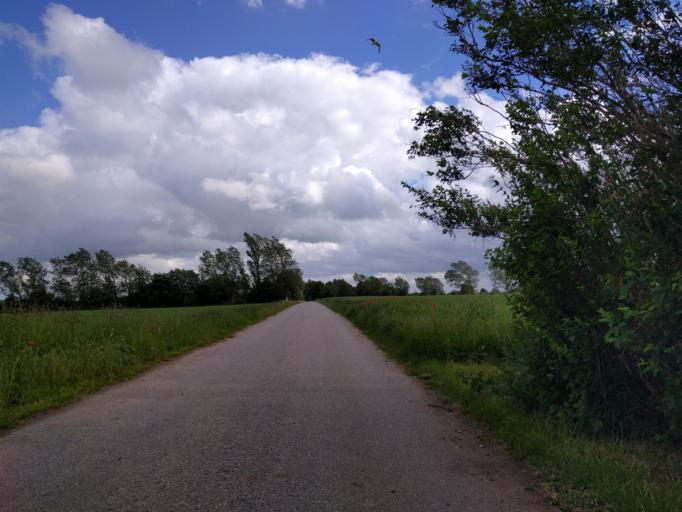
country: DK
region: South Denmark
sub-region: Odense Kommune
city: Bullerup
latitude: 55.4567
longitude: 10.5019
